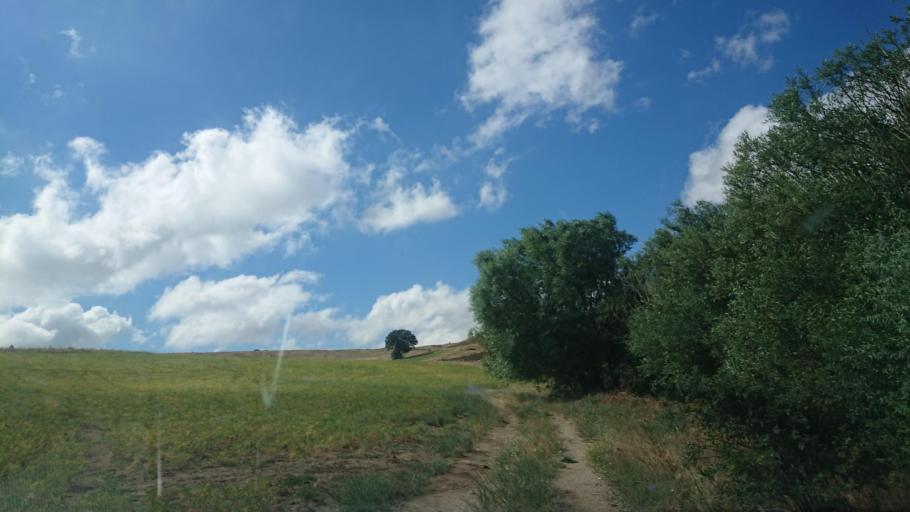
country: TR
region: Aksaray
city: Agacoren
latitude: 38.8425
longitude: 33.9376
